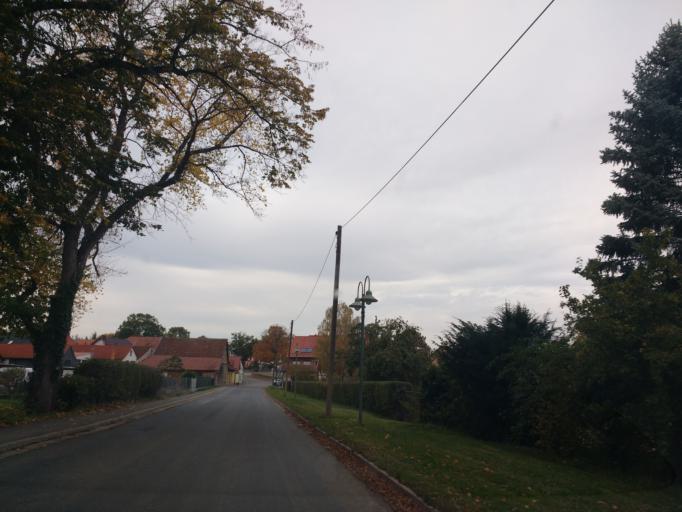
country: DE
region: Thuringia
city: Seebach
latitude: 51.1630
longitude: 10.5157
